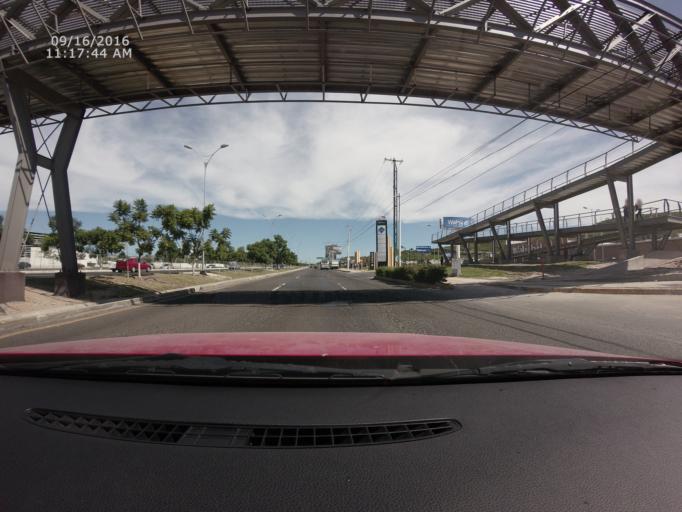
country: MX
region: Queretaro
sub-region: Queretaro
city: El Salitre
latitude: 20.6756
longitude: -100.4340
